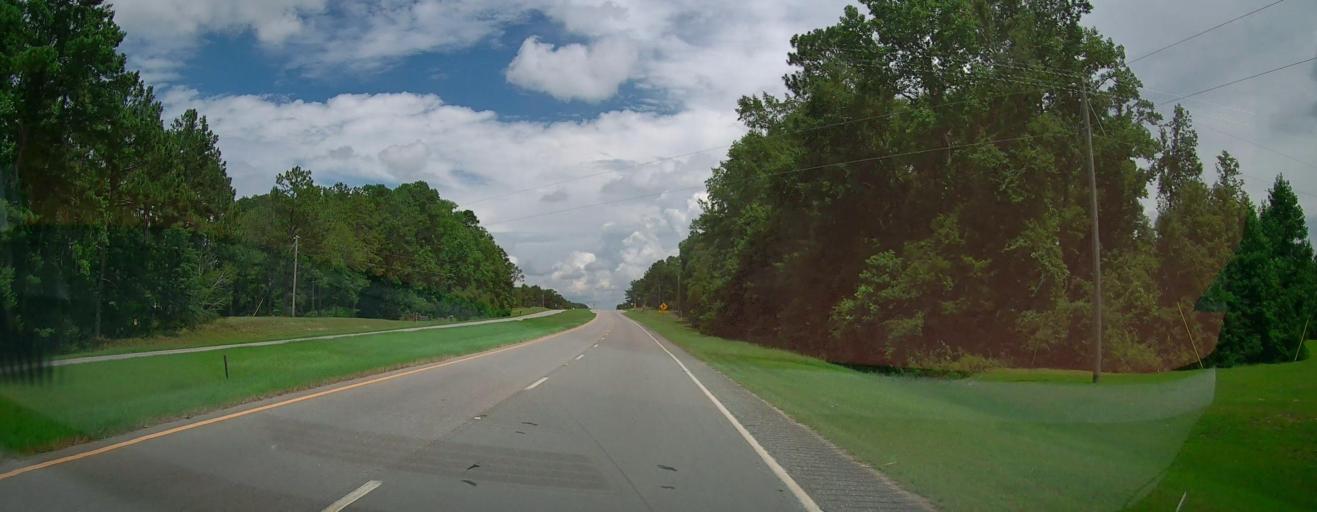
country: US
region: Georgia
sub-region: Dodge County
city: Eastman
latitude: 32.2011
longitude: -83.2531
